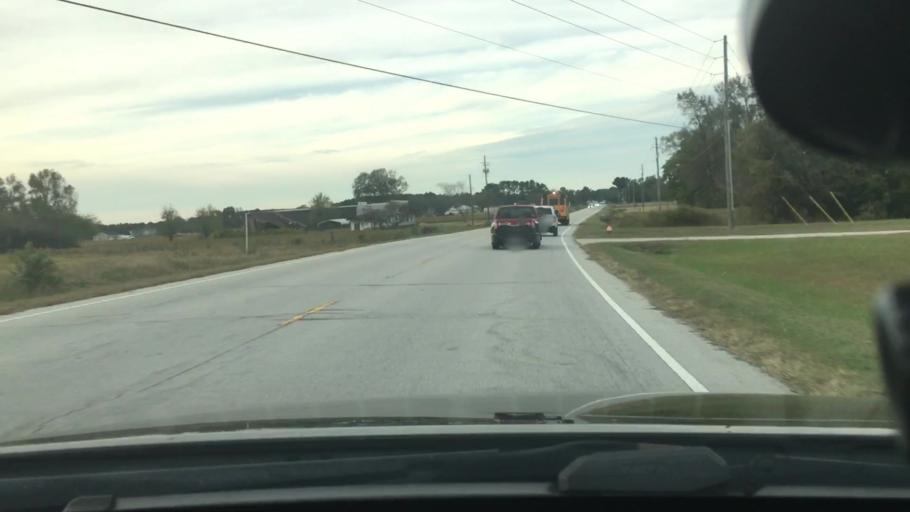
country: US
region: North Carolina
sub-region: Pitt County
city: Windsor
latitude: 35.4993
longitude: -77.3119
